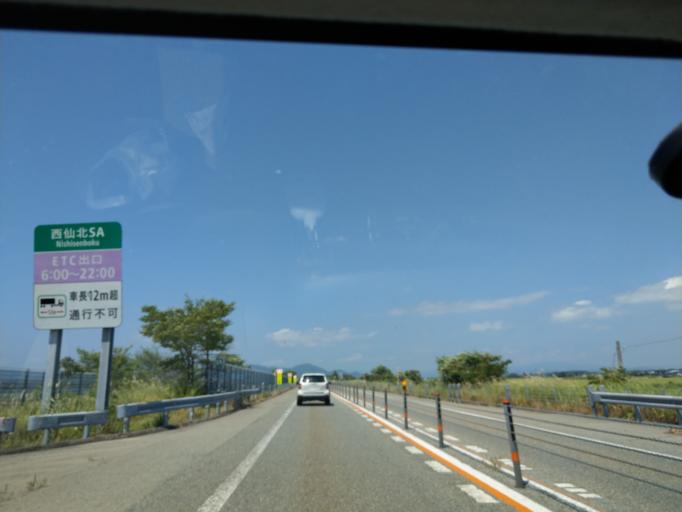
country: JP
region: Akita
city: Omagari
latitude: 39.3761
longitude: 140.4824
